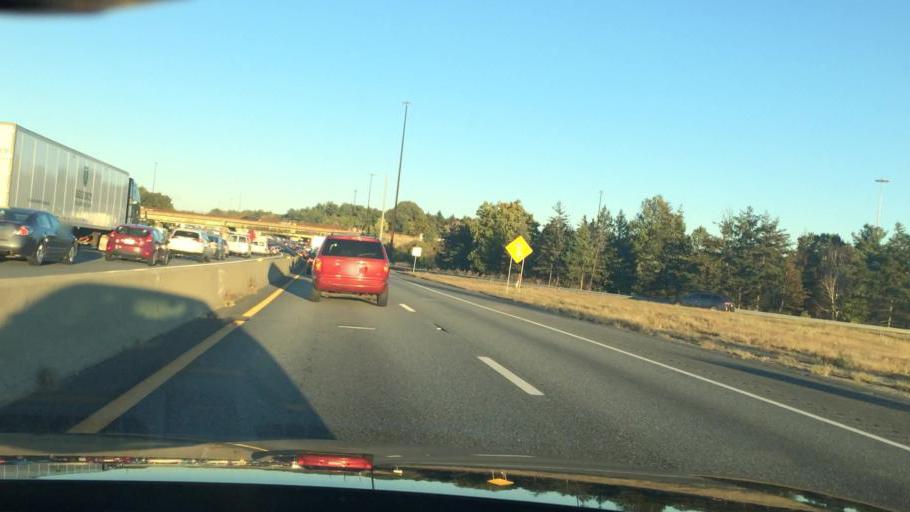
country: US
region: Massachusetts
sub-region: Middlesex County
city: Lowell
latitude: 42.6074
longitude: -71.3230
